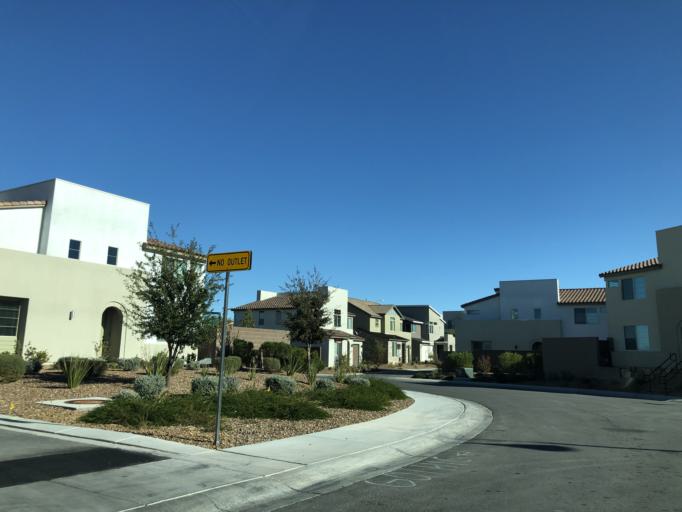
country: US
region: Nevada
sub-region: Clark County
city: Whitney
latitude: 35.9998
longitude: -115.0846
